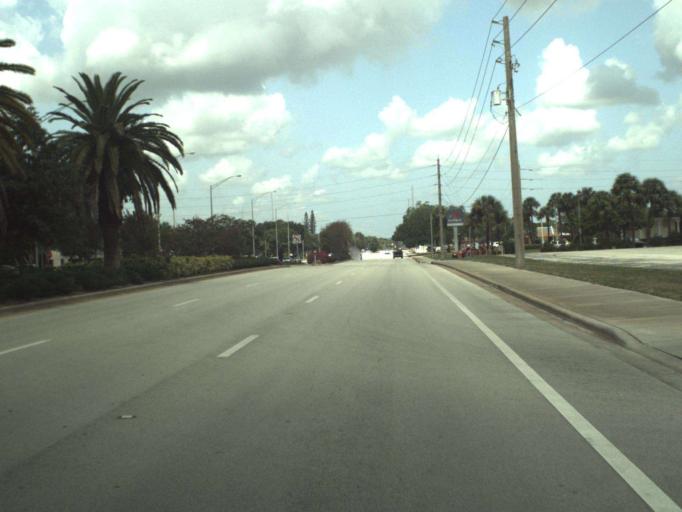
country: US
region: Florida
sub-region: Saint Lucie County
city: Fort Pierce
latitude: 27.4254
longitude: -80.3275
